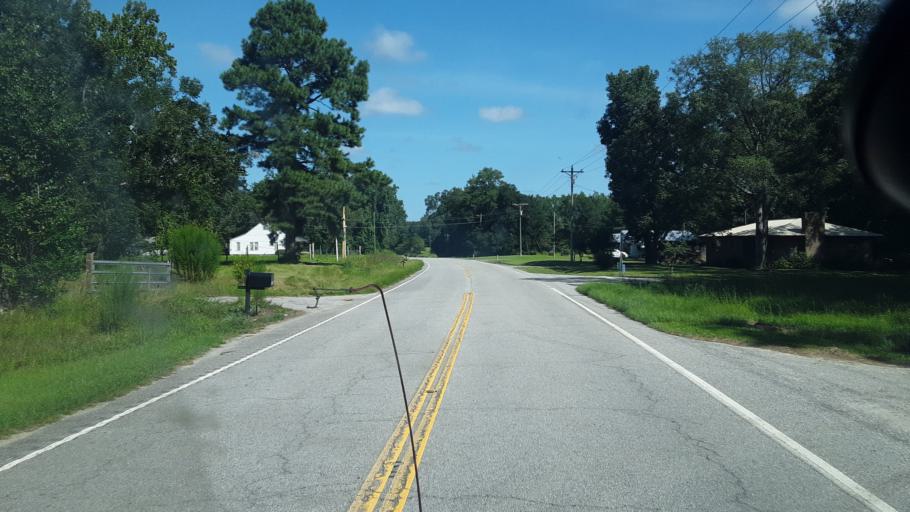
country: US
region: South Carolina
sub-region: Hampton County
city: Varnville
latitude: 32.7740
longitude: -81.0513
